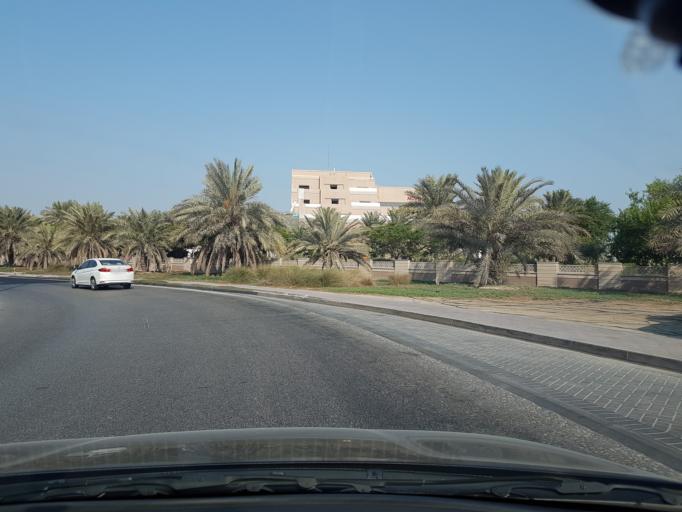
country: BH
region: Muharraq
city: Al Muharraq
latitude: 26.2640
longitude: 50.6244
